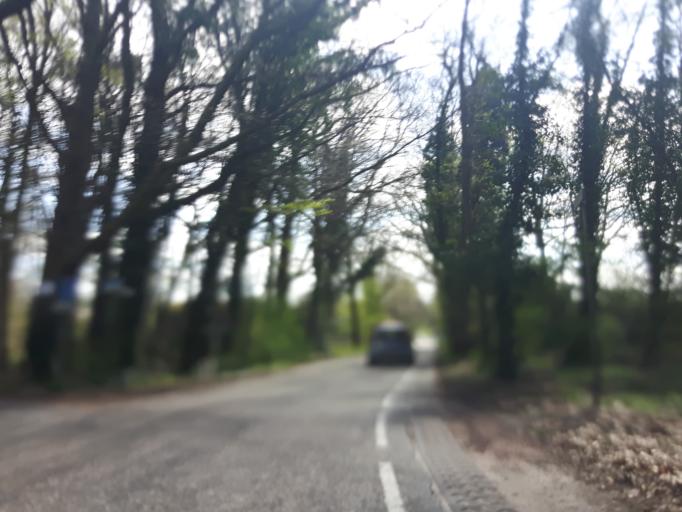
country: NL
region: Overijssel
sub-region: Gemeente Enschede
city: Enschede
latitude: 52.1933
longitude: 6.8318
